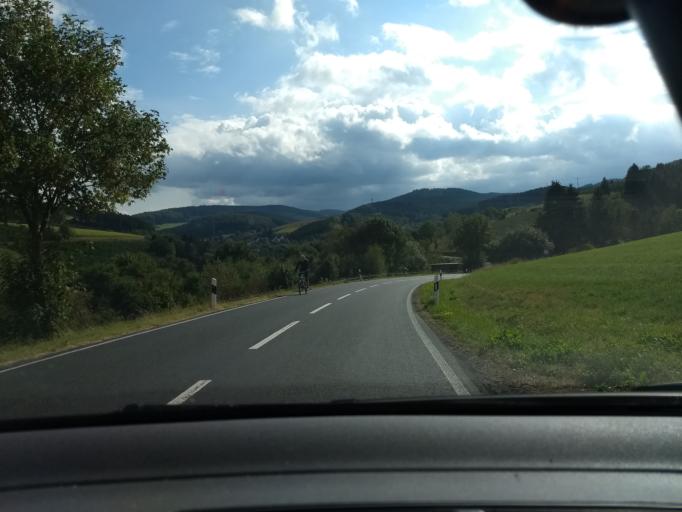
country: DE
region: North Rhine-Westphalia
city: Eslohe
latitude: 51.2421
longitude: 8.1355
